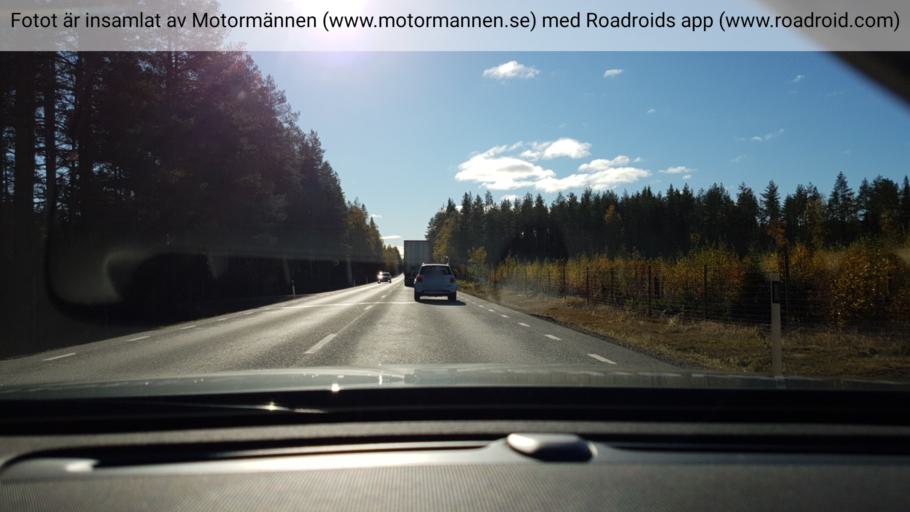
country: SE
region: Vaesterbotten
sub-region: Skelleftea Kommun
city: Burea
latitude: 64.5479
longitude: 21.2486
